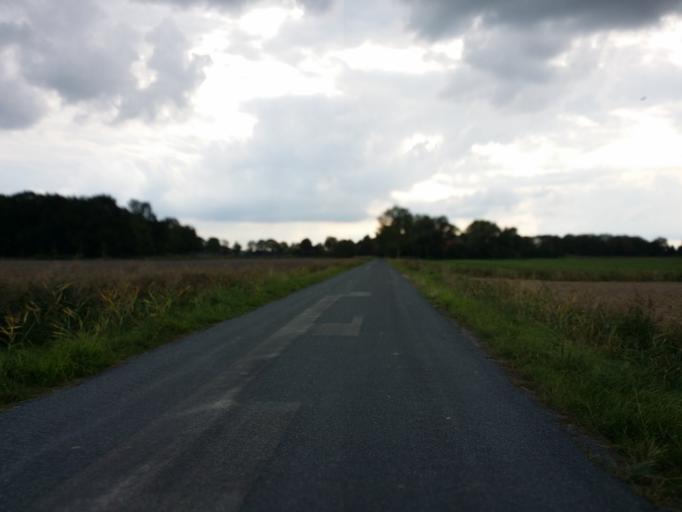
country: DE
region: Lower Saxony
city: Osten
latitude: 53.7198
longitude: 9.1773
